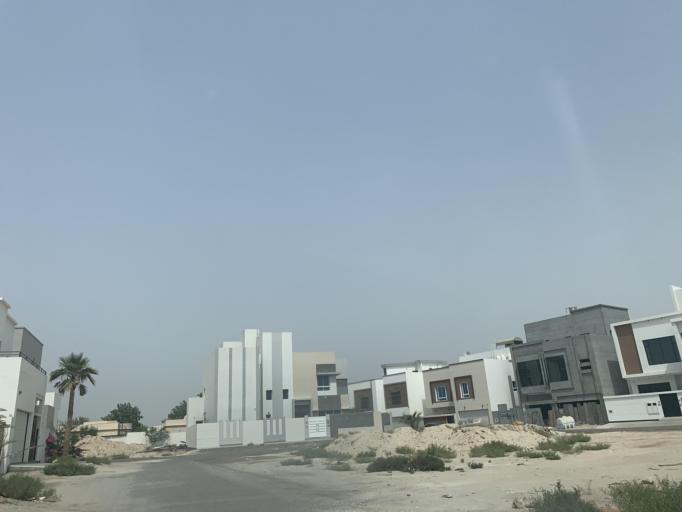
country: BH
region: Manama
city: Jidd Hafs
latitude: 26.1991
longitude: 50.4682
